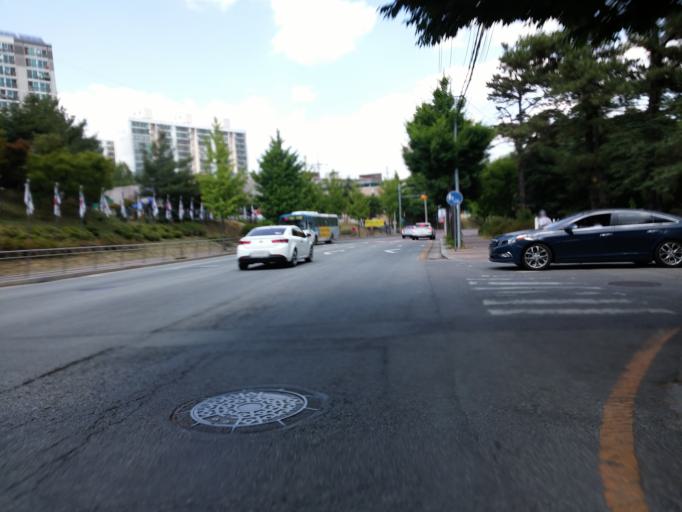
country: KR
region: Chungcheongbuk-do
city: Cheongju-si
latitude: 36.6174
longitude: 127.4743
